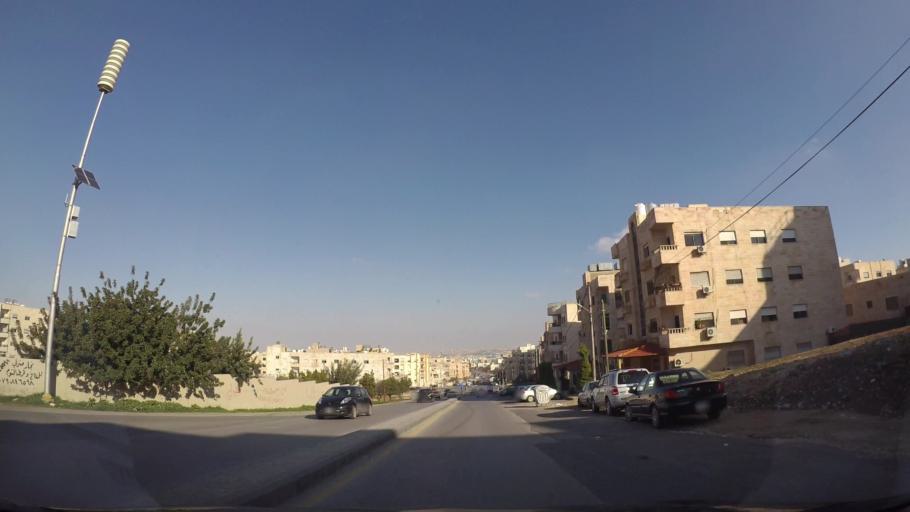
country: JO
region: Amman
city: Amman
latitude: 31.9866
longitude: 35.9410
